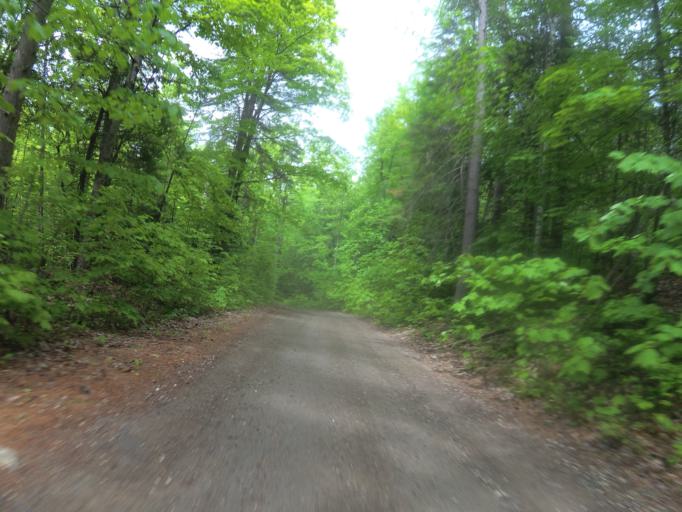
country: CA
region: Ontario
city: Renfrew
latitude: 45.1100
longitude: -76.8243
